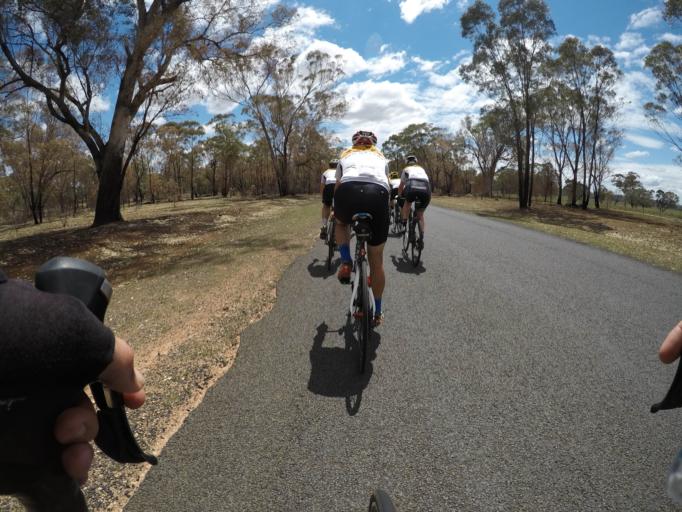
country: AU
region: New South Wales
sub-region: Dubbo Municipality
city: Dubbo
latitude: -32.3976
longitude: 148.5714
